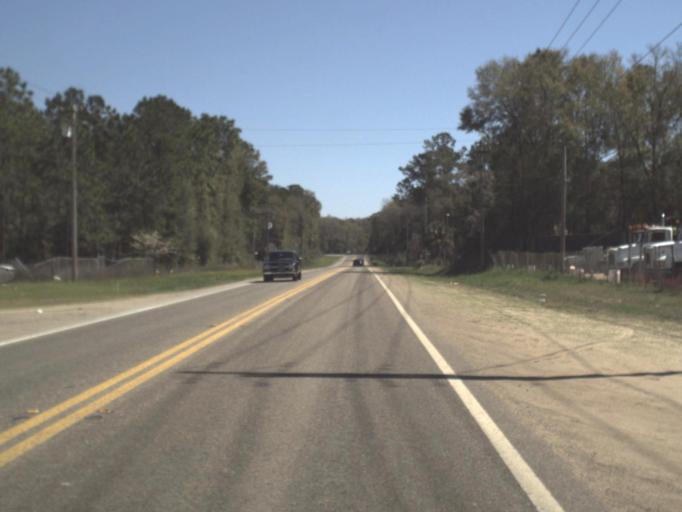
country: US
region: Florida
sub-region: Leon County
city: Tallahassee
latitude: 30.3791
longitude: -84.3019
